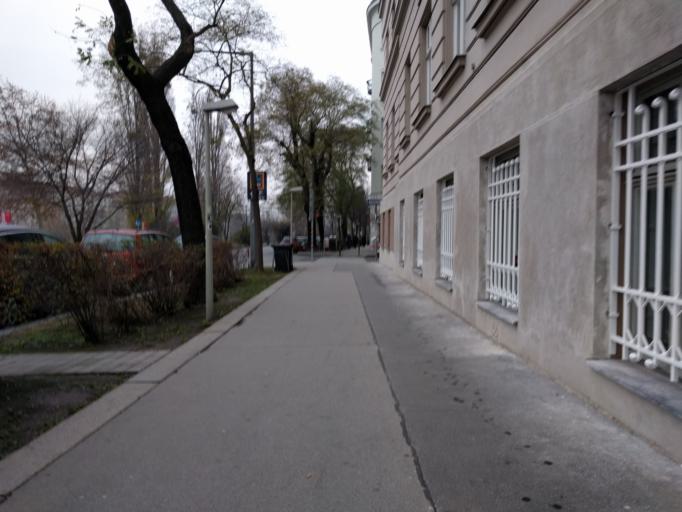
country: AT
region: Vienna
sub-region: Wien Stadt
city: Vienna
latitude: 48.2282
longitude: 16.3655
